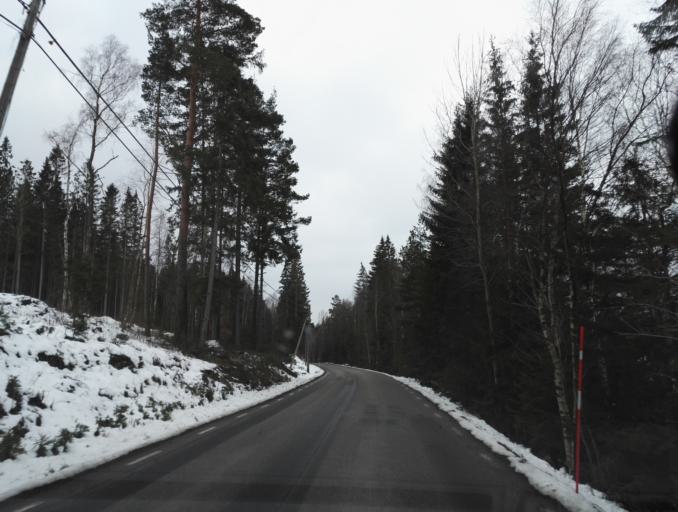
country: SE
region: Vaestra Goetaland
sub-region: Alingsas Kommun
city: Ingared
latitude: 57.7737
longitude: 12.4926
